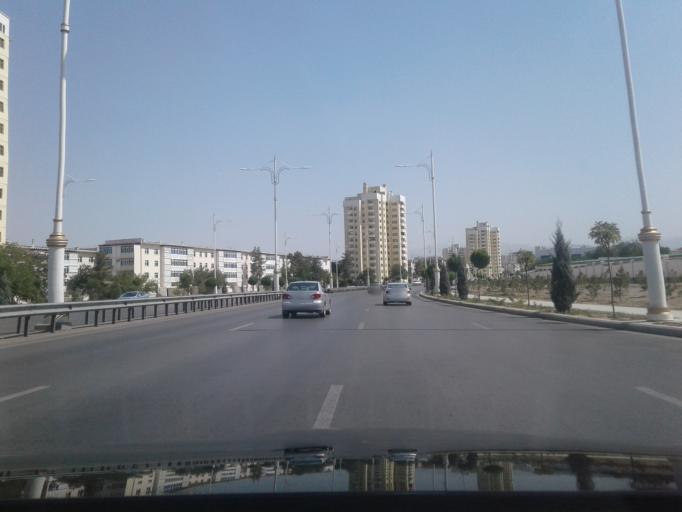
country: TM
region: Ahal
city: Ashgabat
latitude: 37.9187
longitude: 58.3890
